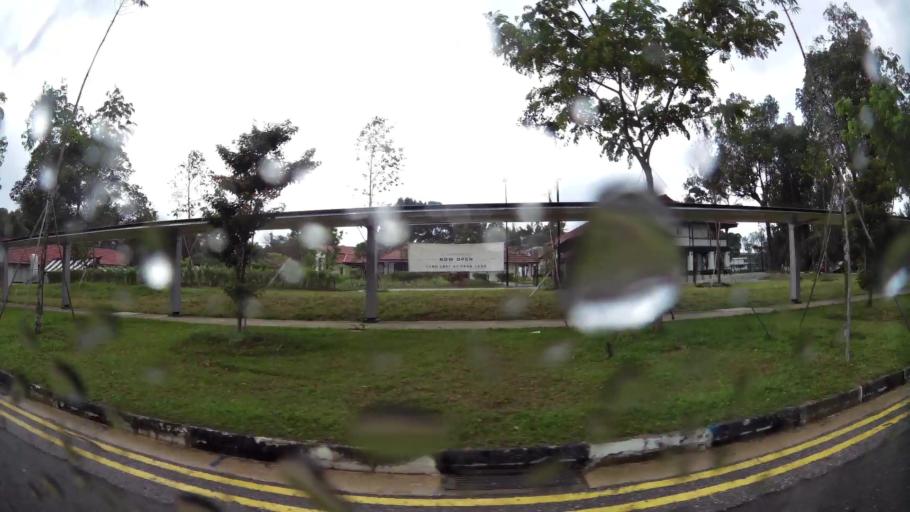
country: MY
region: Johor
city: Kampung Pasir Gudang Baru
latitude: 1.4075
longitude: 103.8685
